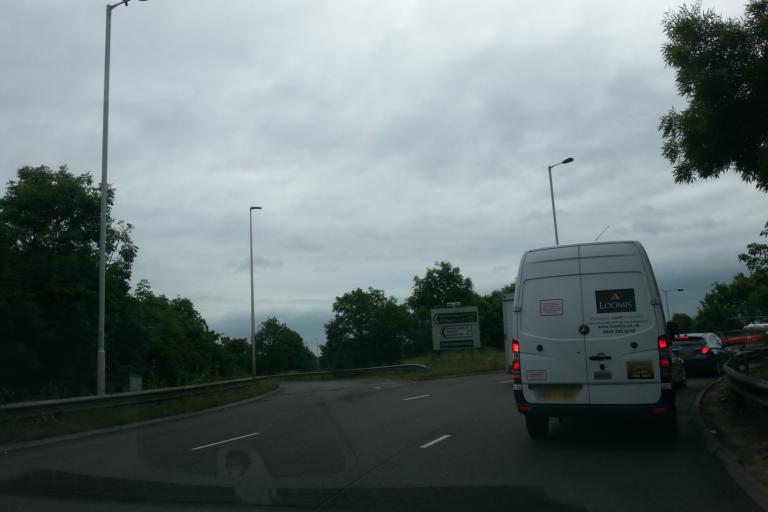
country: GB
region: England
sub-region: Cambridgeshire
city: Yaxley
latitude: 52.5463
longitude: -0.2648
